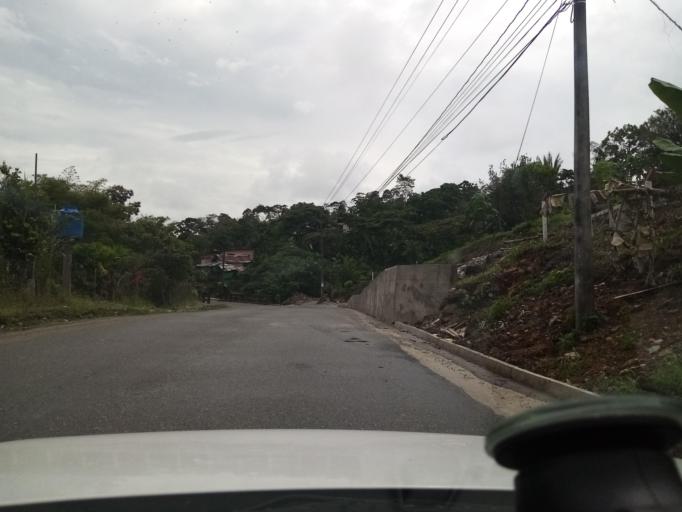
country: EC
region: Napo
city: Tena
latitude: -1.0396
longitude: -77.7869
